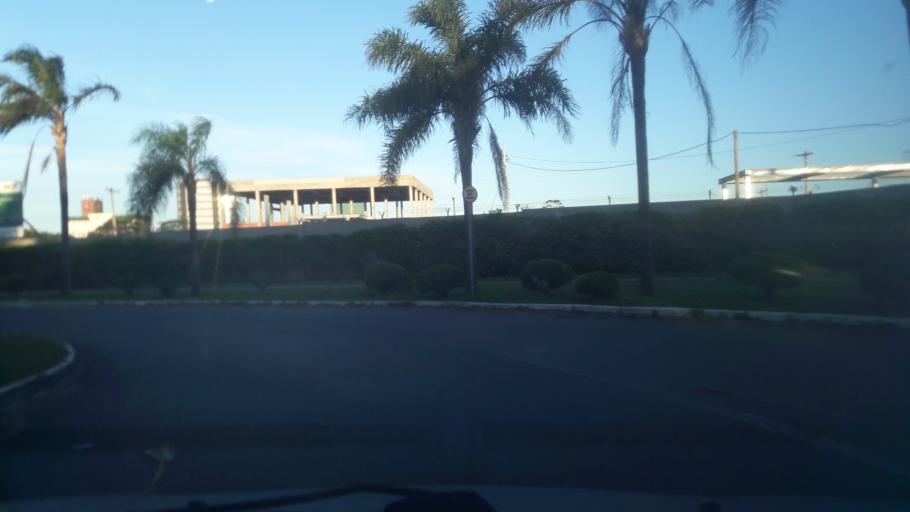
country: BR
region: Rio Grande do Sul
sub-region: Porto Alegre
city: Porto Alegre
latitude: -29.9897
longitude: -51.1741
